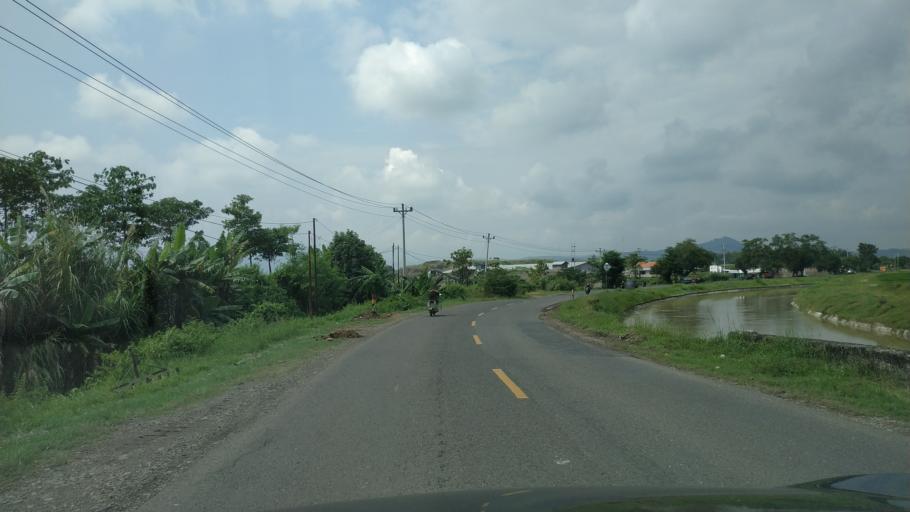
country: ID
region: Central Java
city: Margasari
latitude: -7.0847
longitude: 108.9838
